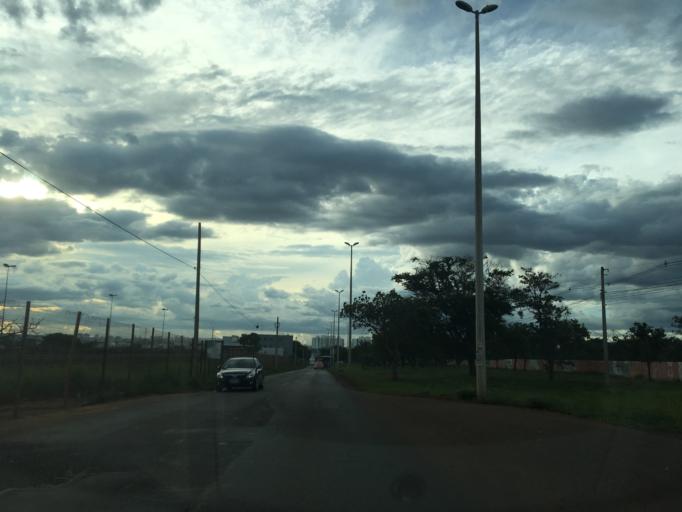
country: BR
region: Federal District
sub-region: Brasilia
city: Brasilia
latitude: -15.8324
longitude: -47.9463
